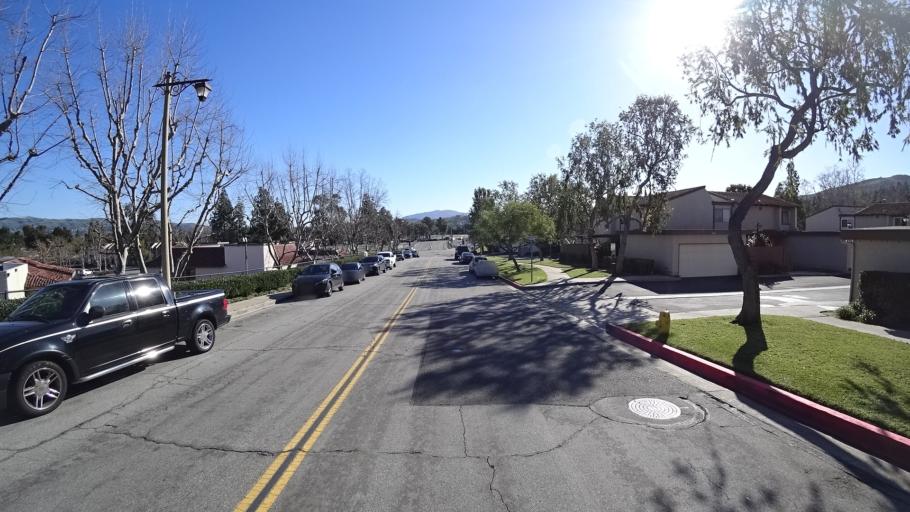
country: US
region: California
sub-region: Orange County
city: Villa Park
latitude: 33.8490
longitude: -117.7916
